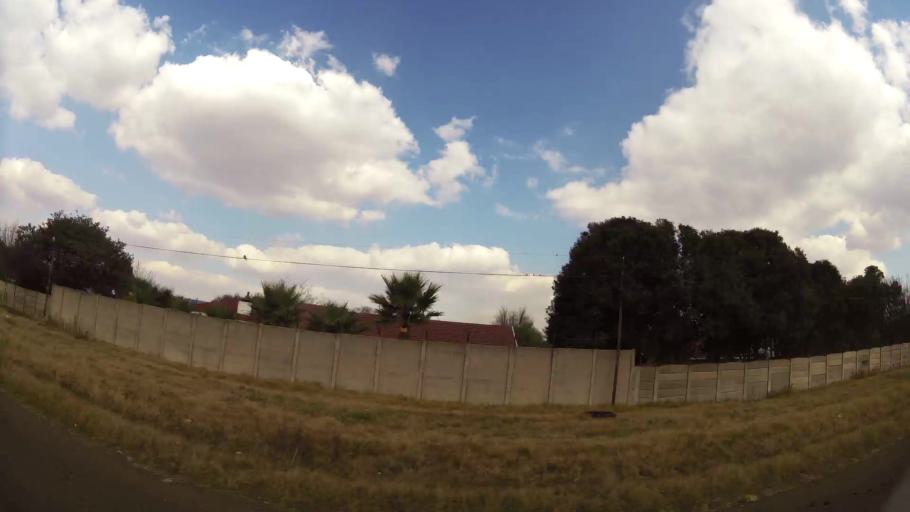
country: ZA
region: Mpumalanga
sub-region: Nkangala District Municipality
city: Delmas
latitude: -26.1402
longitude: 28.6707
